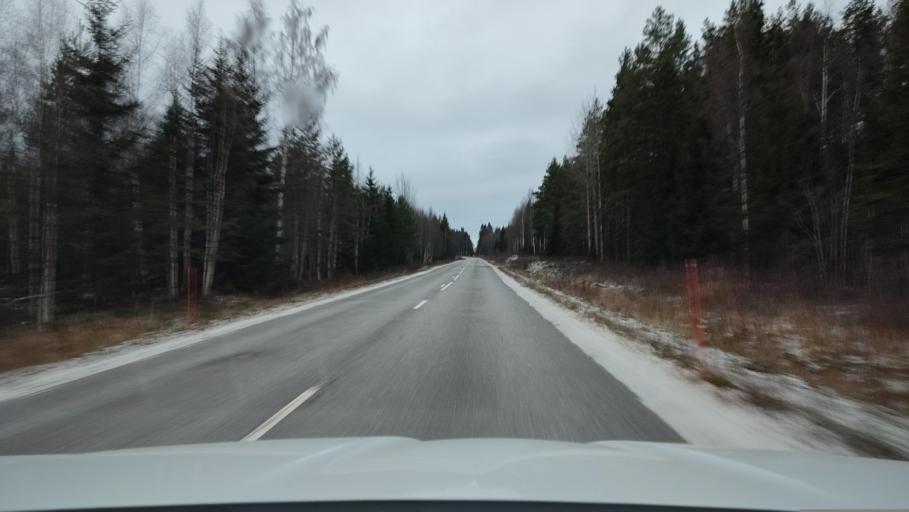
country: FI
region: Ostrobothnia
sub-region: Vaasa
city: Replot
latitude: 63.2616
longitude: 21.3615
